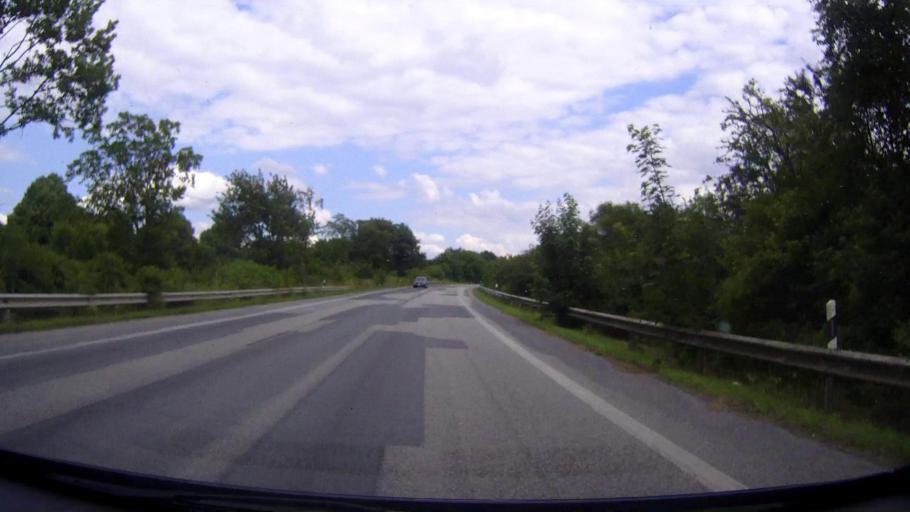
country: DE
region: Schleswig-Holstein
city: Badendorf
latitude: 53.8983
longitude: 10.5908
